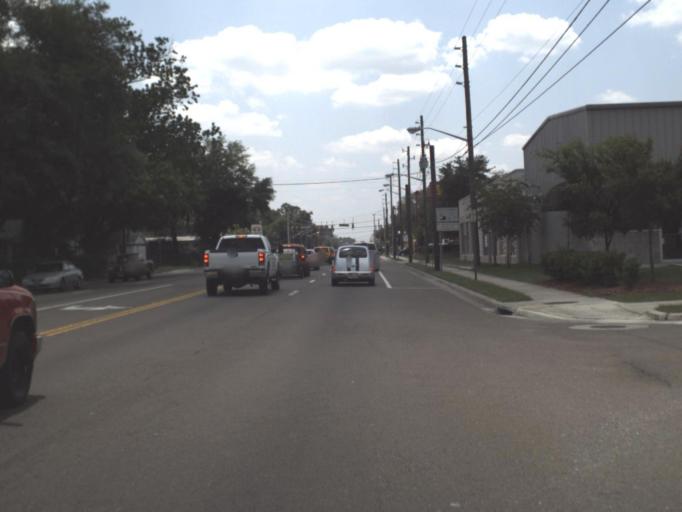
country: US
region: Florida
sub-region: Duval County
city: Jacksonville
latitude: 30.3085
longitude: -81.7307
